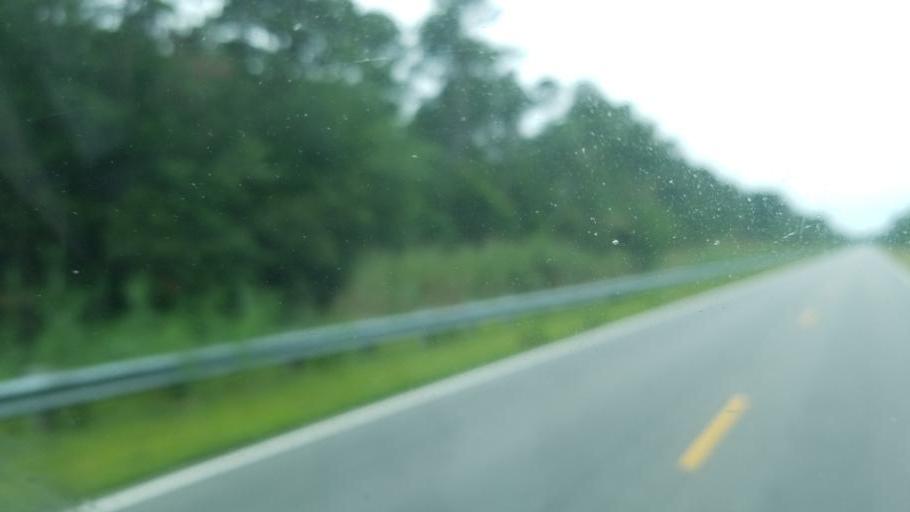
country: US
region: North Carolina
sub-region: Tyrrell County
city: Columbia
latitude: 35.9238
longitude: -76.1342
